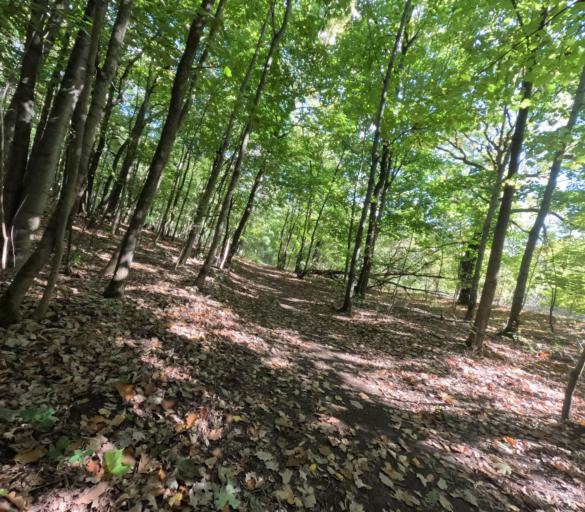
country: DE
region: Saxony
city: Albertstadt
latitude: 51.1076
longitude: 13.7401
